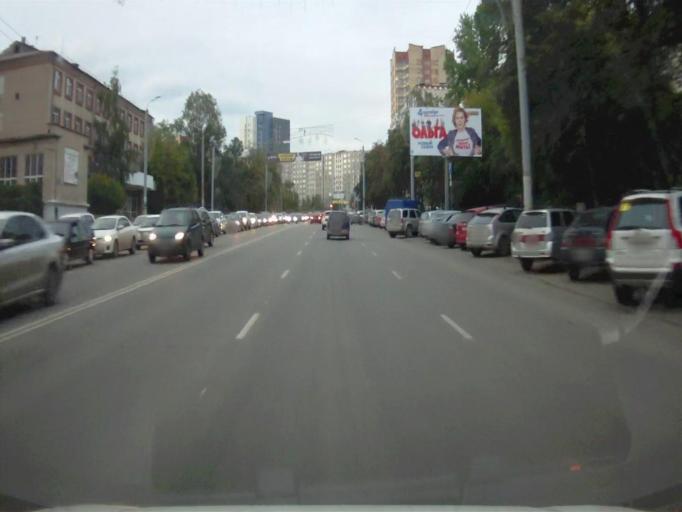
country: RU
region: Chelyabinsk
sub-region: Gorod Chelyabinsk
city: Chelyabinsk
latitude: 55.1562
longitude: 61.3815
